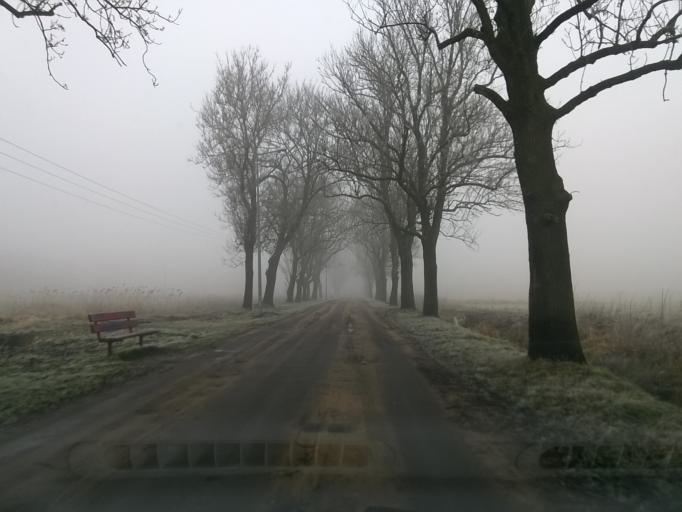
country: PL
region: Kujawsko-Pomorskie
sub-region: Powiat nakielski
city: Naklo nad Notecia
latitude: 53.1330
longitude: 17.6052
